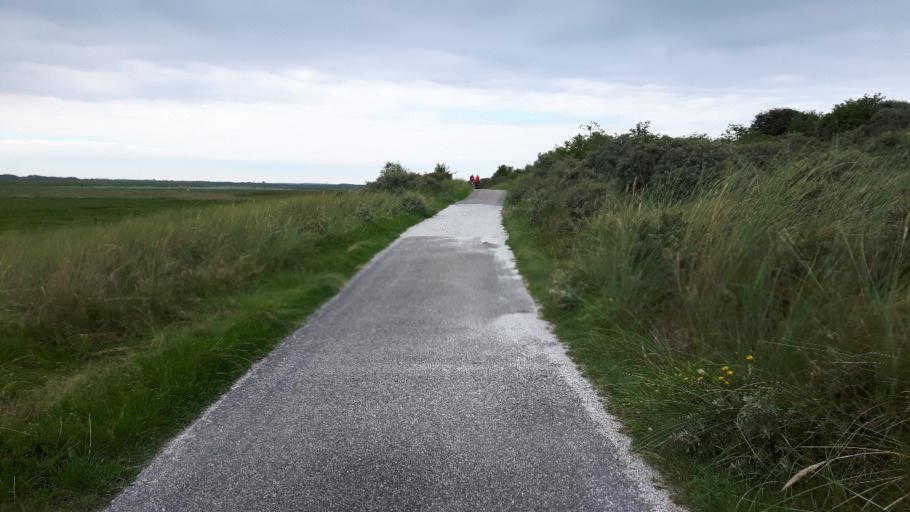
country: NL
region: Friesland
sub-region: Gemeente Dongeradeel
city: Holwerd
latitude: 53.4605
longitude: 5.8744
